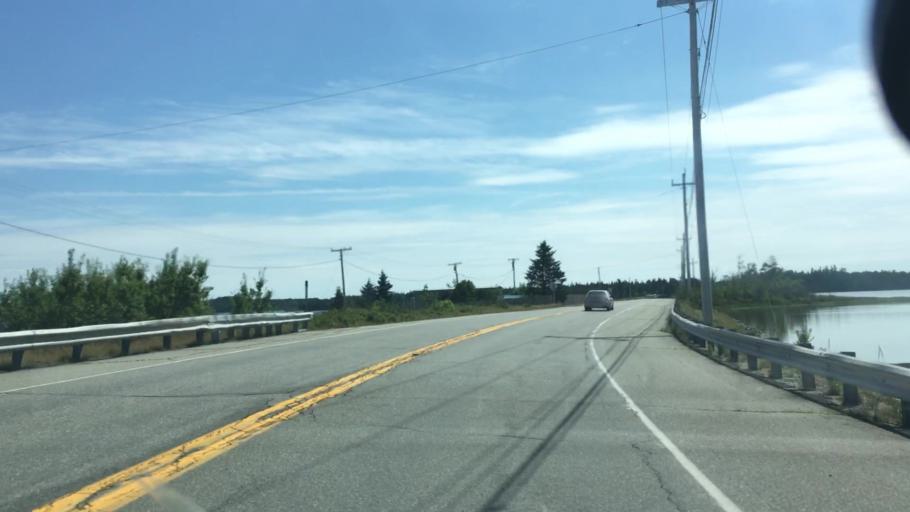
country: US
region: Maine
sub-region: Washington County
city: Eastport
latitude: 44.9534
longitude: -67.0395
